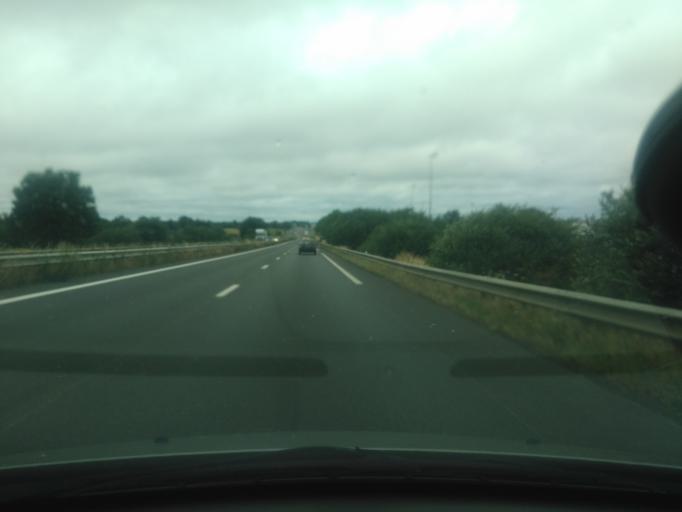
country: FR
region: Brittany
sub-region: Departement des Cotes-d'Armor
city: Lamballe
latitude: 48.4624
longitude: -2.5409
